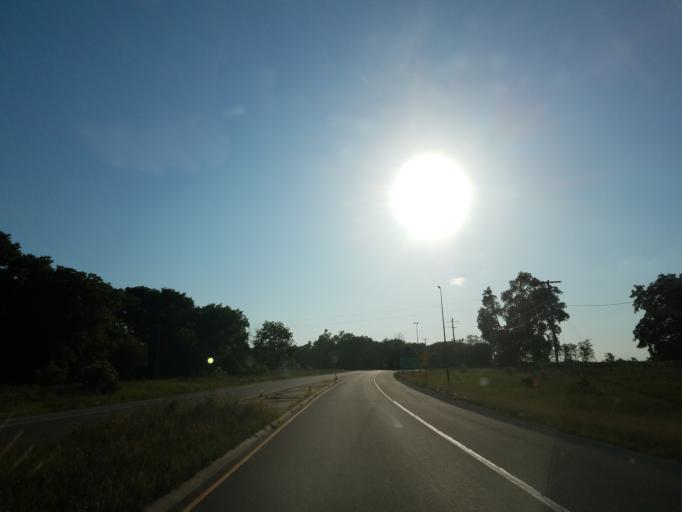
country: US
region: Illinois
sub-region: McLean County
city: Twin Grove
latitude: 40.4084
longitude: -89.0574
